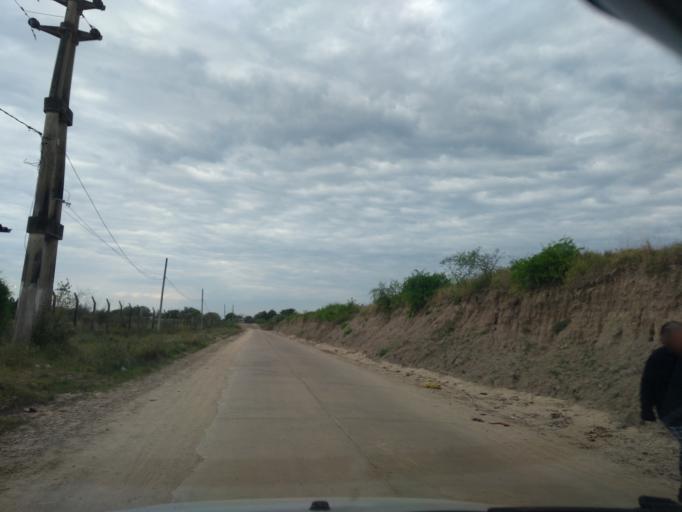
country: AR
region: Chaco
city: Puerto Vilelas
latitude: -27.5363
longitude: -58.9191
